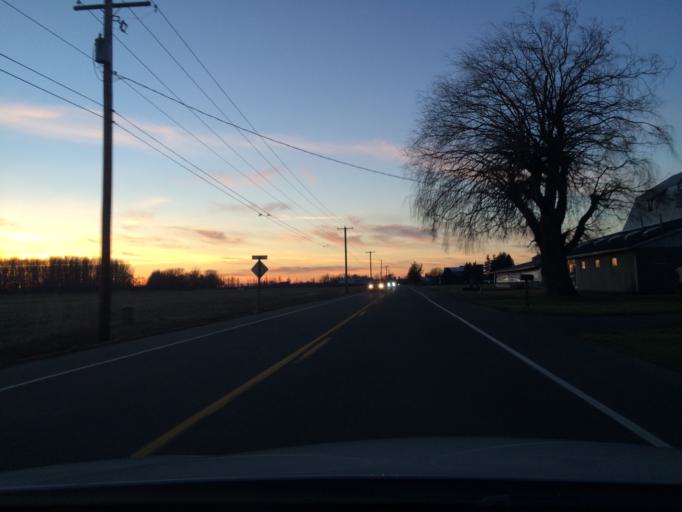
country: US
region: Washington
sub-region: Whatcom County
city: Lynden
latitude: 48.9421
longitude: -122.4104
